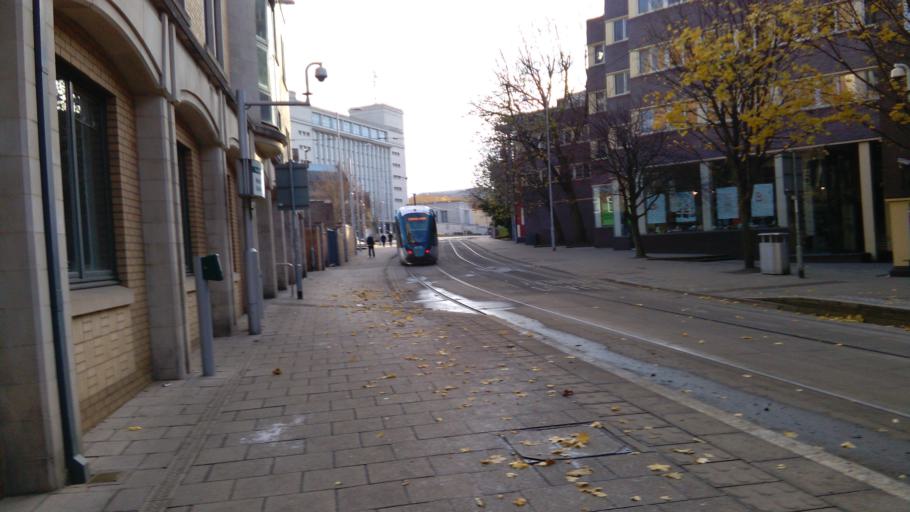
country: GB
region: England
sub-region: Nottingham
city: Nottingham
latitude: 52.9579
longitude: -1.1550
